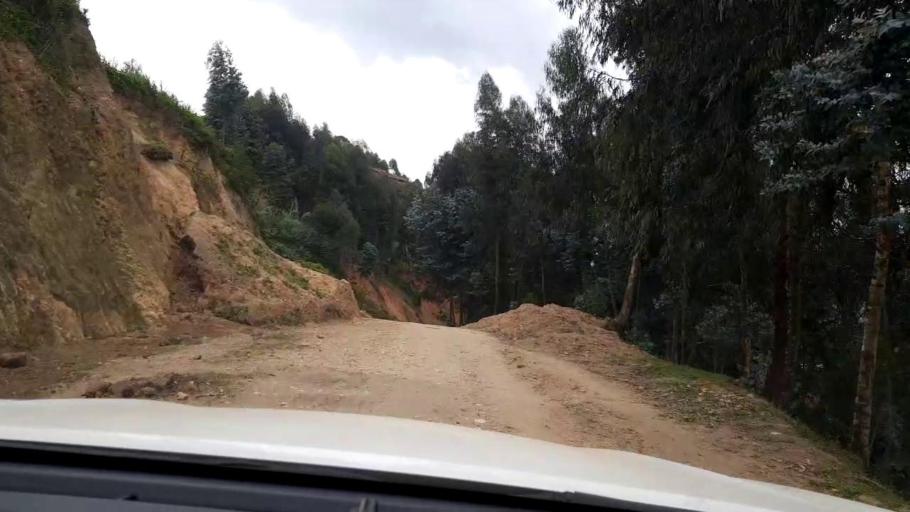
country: RW
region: Western Province
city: Kibuye
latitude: -1.8323
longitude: 29.5453
